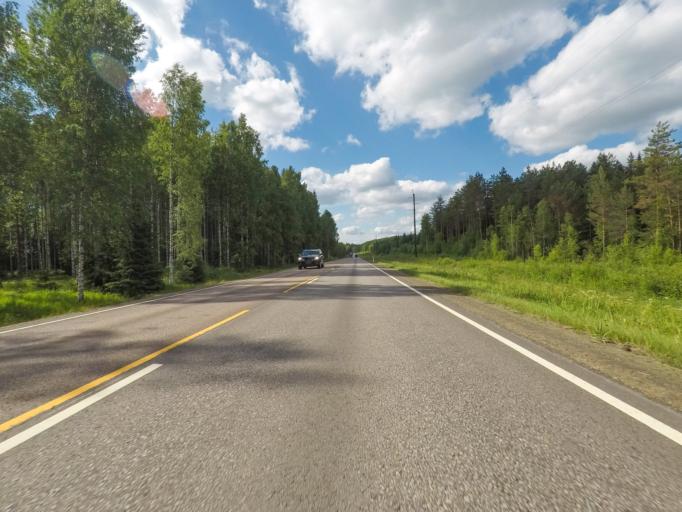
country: FI
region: Southern Savonia
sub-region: Savonlinna
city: Kerimaeki
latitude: 61.8555
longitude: 29.1637
